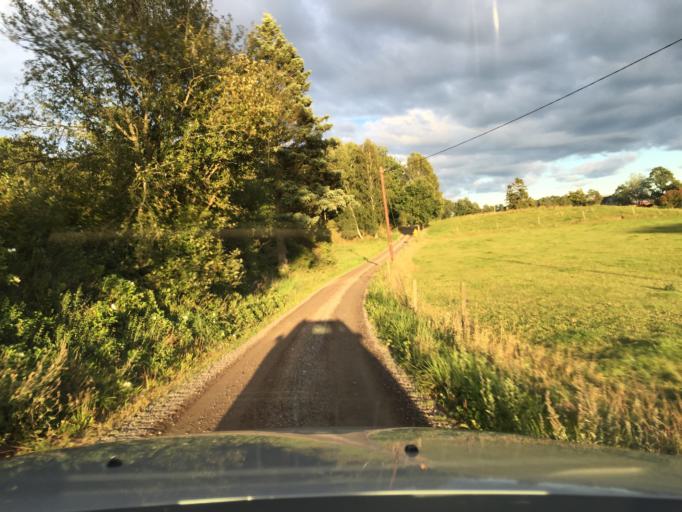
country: SE
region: Skane
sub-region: Hassleholms Kommun
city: Sosdala
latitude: 56.0277
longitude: 13.7439
